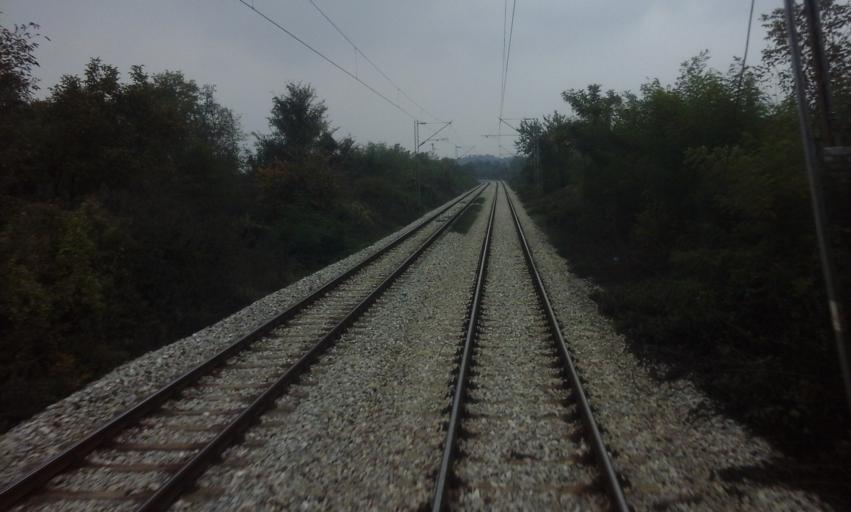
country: RS
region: Central Serbia
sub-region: Sumadijski Okrug
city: Lapovo
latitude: 44.2121
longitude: 21.0936
